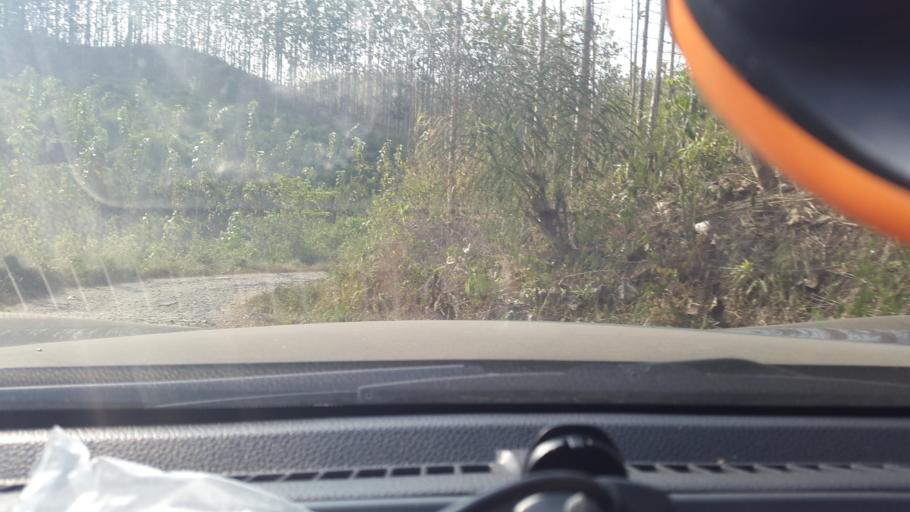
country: ID
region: West Java
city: Cikupa
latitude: -7.3579
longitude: 106.7039
